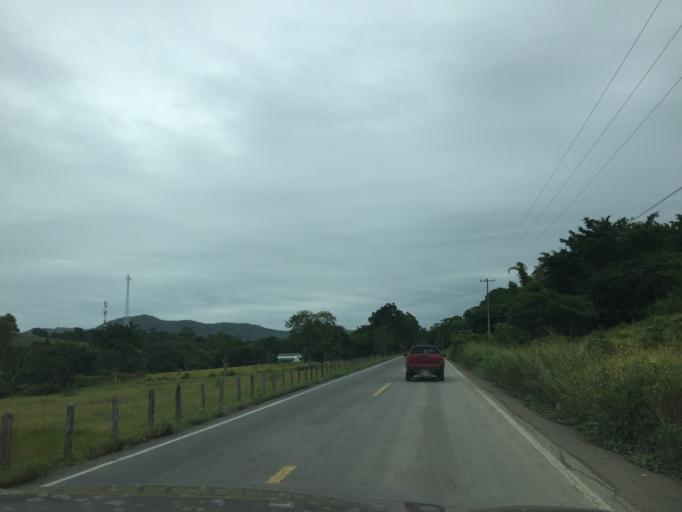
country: MX
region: Veracruz
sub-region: Papantla
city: El Chote
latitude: 20.4398
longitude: -97.3994
